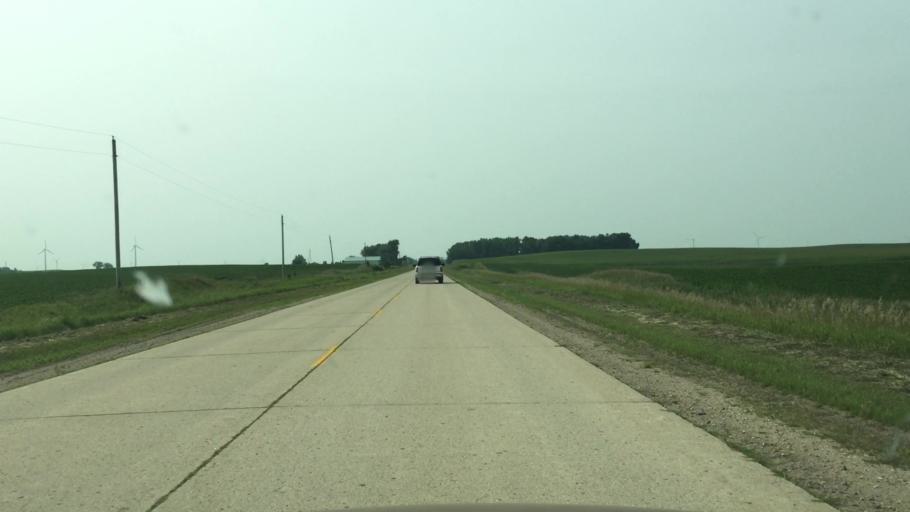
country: US
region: Iowa
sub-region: Dickinson County
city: Lake Park
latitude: 43.4264
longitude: -95.2891
